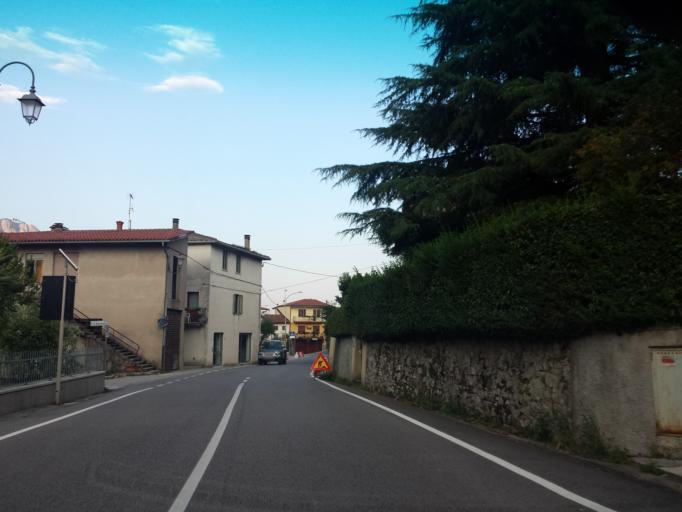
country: IT
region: Veneto
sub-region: Provincia di Vicenza
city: Velo d'Astico
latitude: 45.7885
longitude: 11.3670
